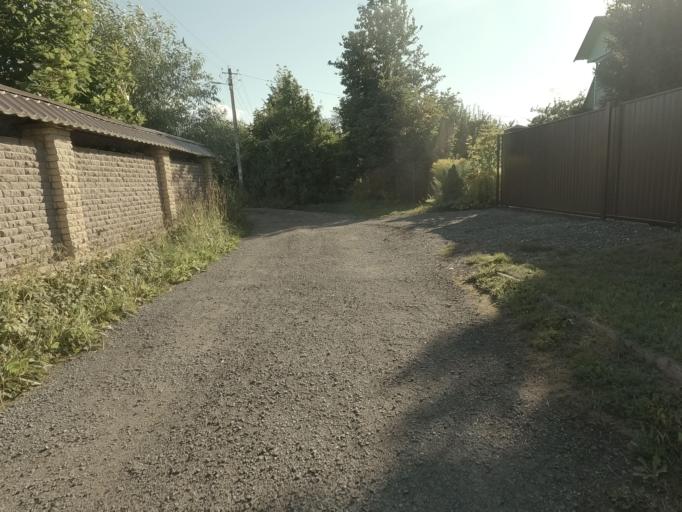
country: RU
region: Leningrad
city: Kirovsk
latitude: 59.9267
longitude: 30.9805
